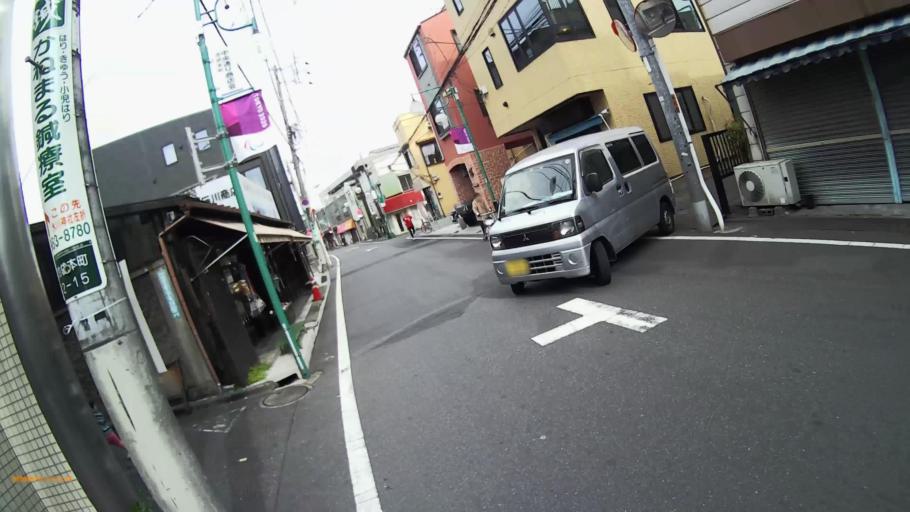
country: JP
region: Tokyo
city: Tokyo
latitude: 35.7409
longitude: 139.7120
